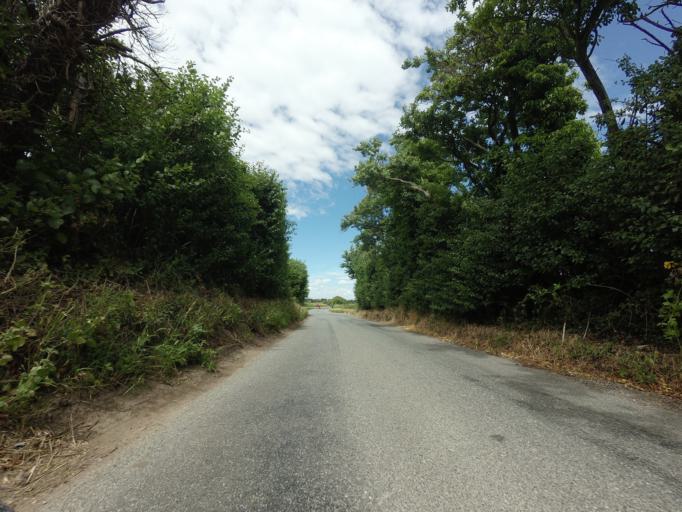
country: GB
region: England
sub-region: Kent
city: Strood
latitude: 51.4239
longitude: 0.4802
